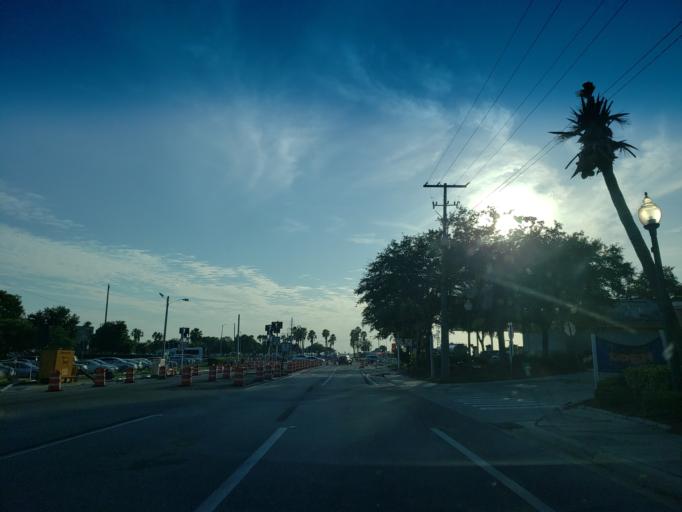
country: US
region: Florida
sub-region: Sarasota County
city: Sarasota
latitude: 27.3450
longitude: -82.5456
